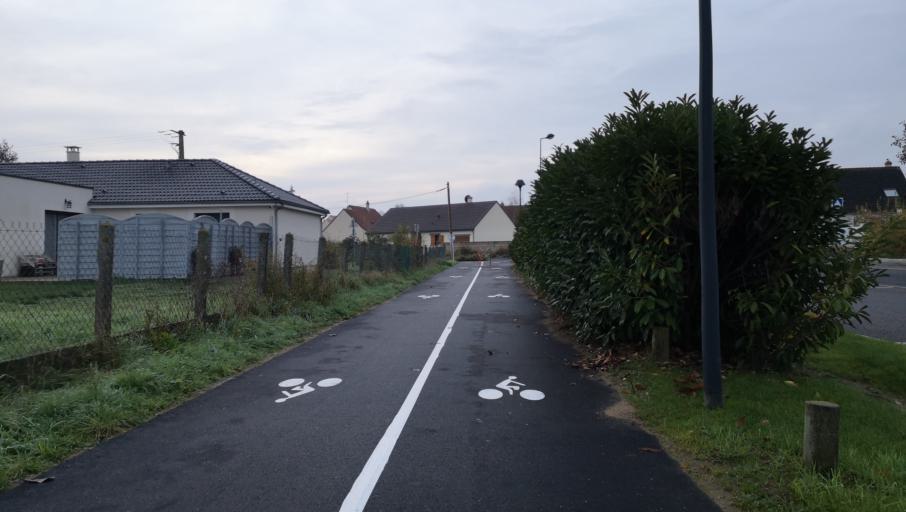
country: FR
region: Centre
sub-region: Departement du Loiret
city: Semoy
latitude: 47.9368
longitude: 1.9488
